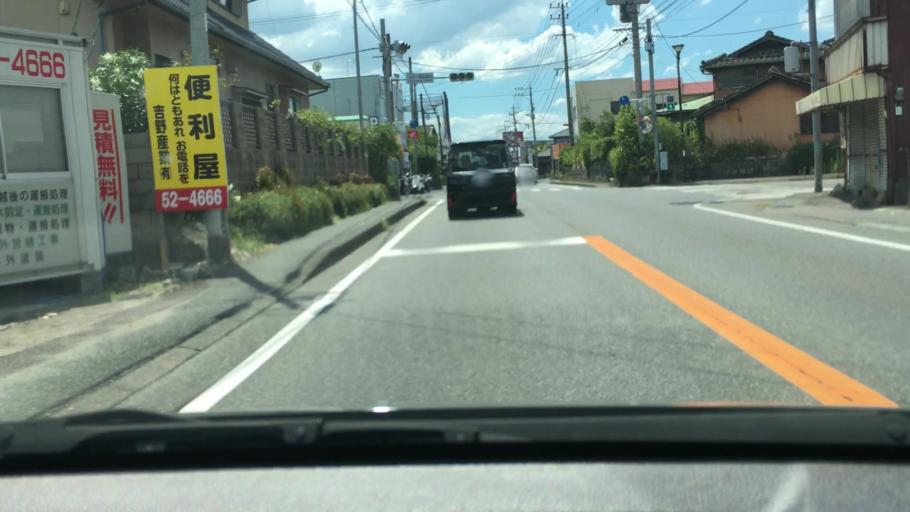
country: JP
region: Saga Prefecture
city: Kanzakimachi-kanzaki
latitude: 33.3245
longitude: 130.4017
